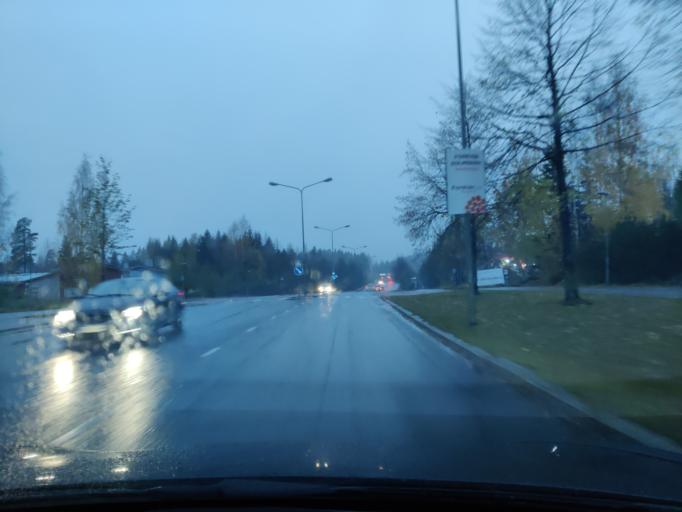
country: FI
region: Northern Savo
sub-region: Kuopio
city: Kuopio
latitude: 62.8360
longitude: 27.6601
